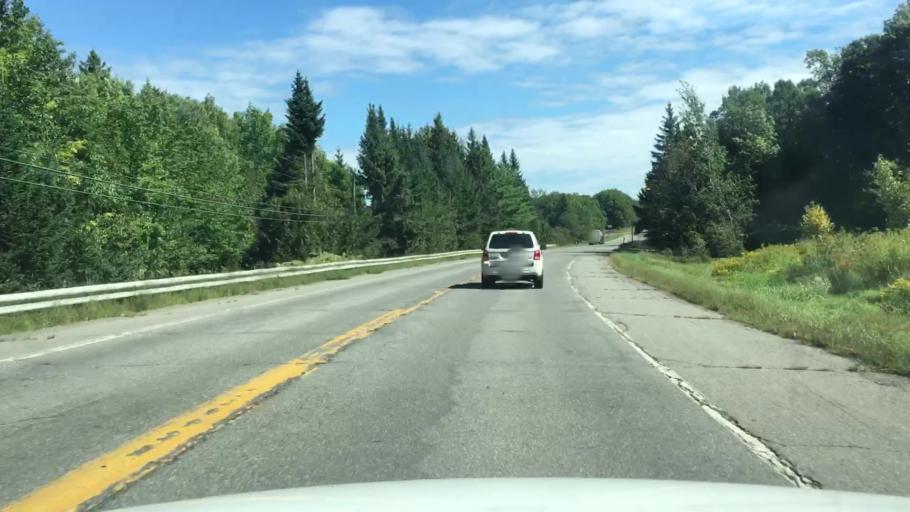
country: US
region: Maine
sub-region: Penobscot County
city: Dexter
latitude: 45.0473
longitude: -69.2701
